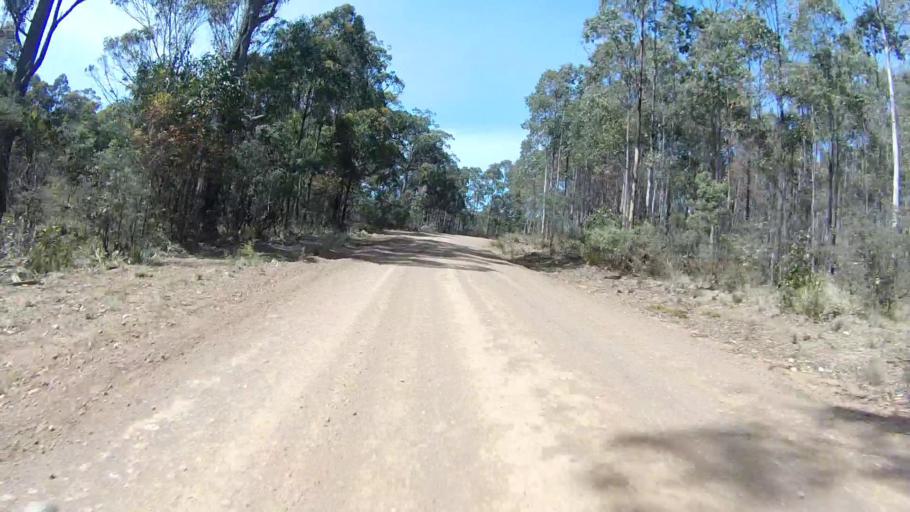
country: AU
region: Tasmania
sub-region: Sorell
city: Sorell
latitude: -42.6681
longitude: 147.7303
